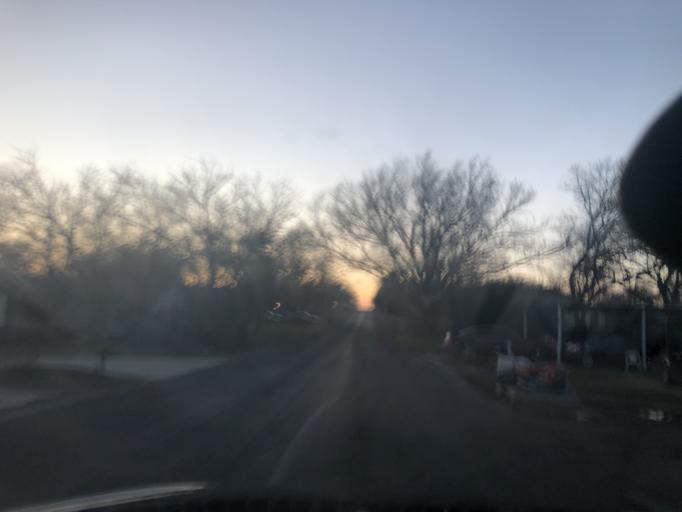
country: US
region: Texas
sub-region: Tarrant County
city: White Settlement
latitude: 32.7282
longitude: -97.4917
